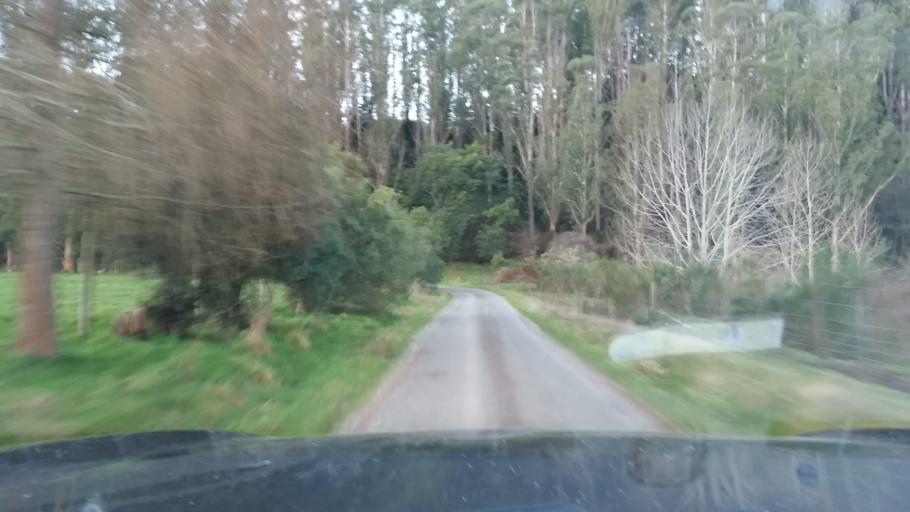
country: NZ
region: Marlborough
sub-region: Marlborough District
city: Blenheim
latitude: -41.4722
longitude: 173.7446
